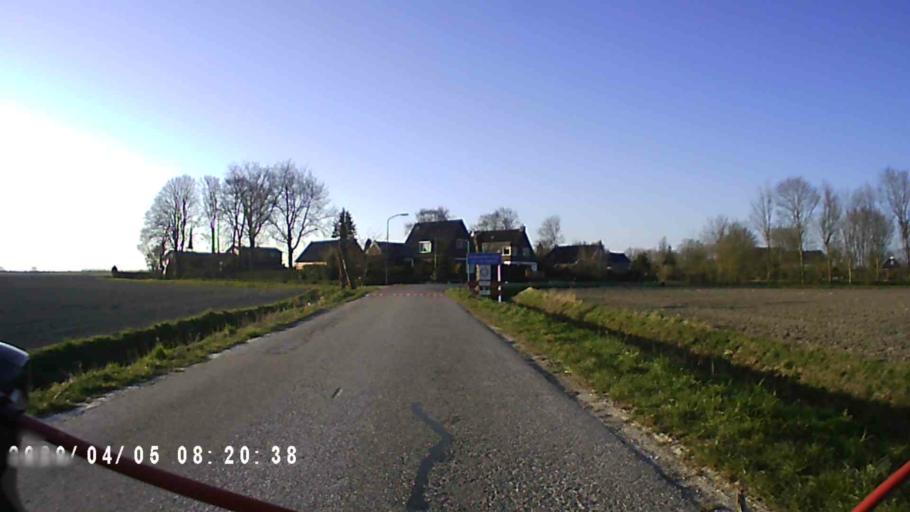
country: NL
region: Groningen
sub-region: Gemeente Zuidhorn
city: Oldehove
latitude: 53.3350
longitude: 6.4506
